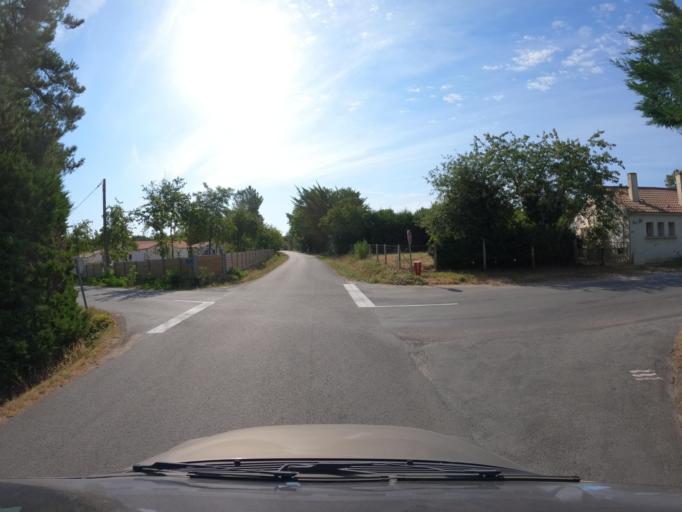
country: FR
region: Pays de la Loire
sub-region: Departement de la Vendee
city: Soullans
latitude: 46.8040
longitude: -1.8759
